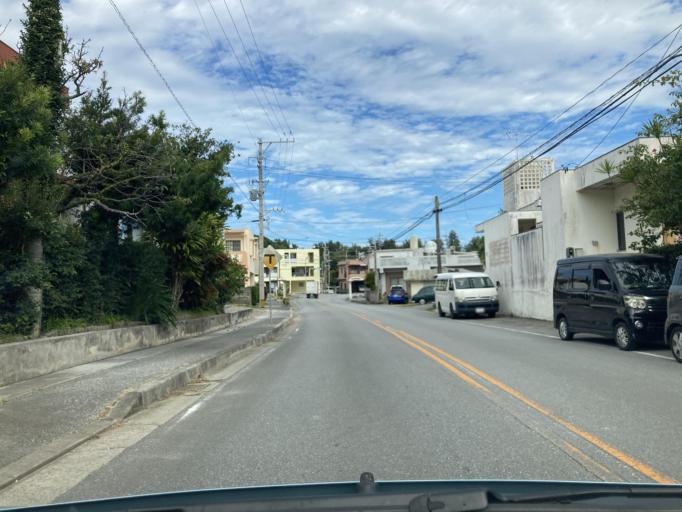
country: JP
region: Okinawa
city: Ishikawa
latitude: 26.4363
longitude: 127.7782
